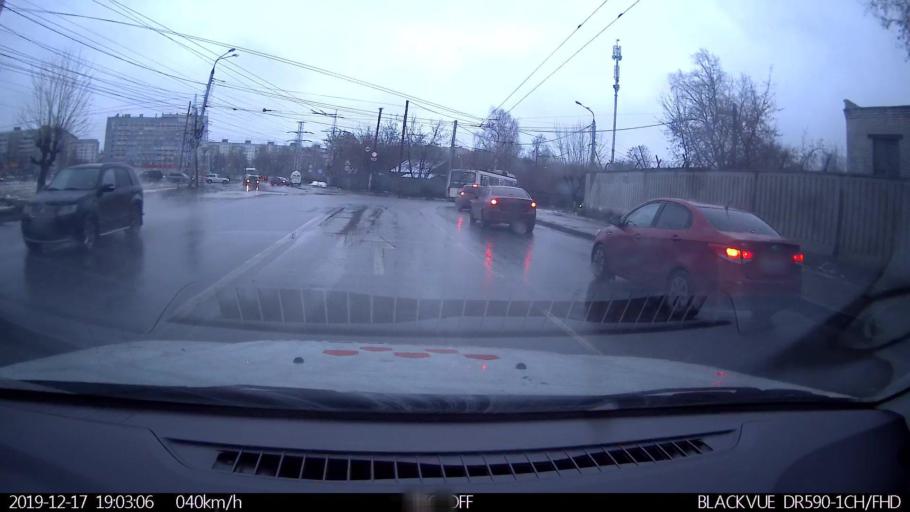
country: RU
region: Nizjnij Novgorod
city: Nizhniy Novgorod
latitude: 56.3306
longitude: 43.8669
